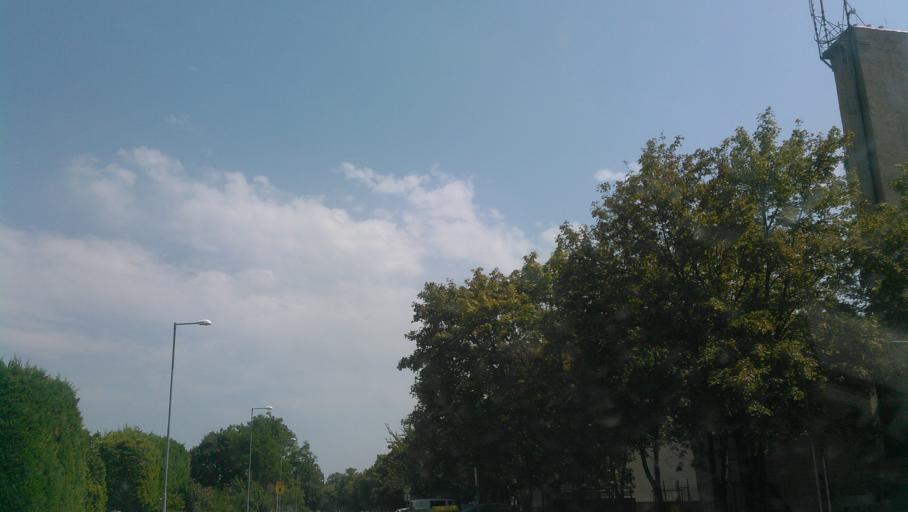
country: SK
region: Trnavsky
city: Dunajska Streda
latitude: 48.0009
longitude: 17.6053
